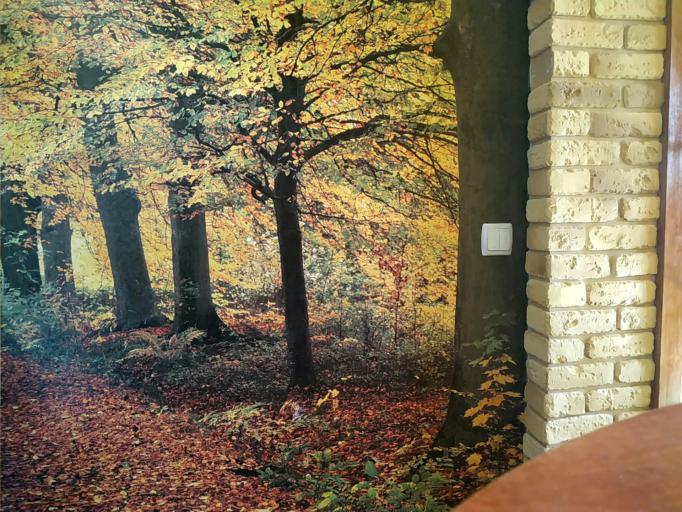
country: RU
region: Jaroslavl
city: Kukoboy
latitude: 58.8576
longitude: 39.7316
